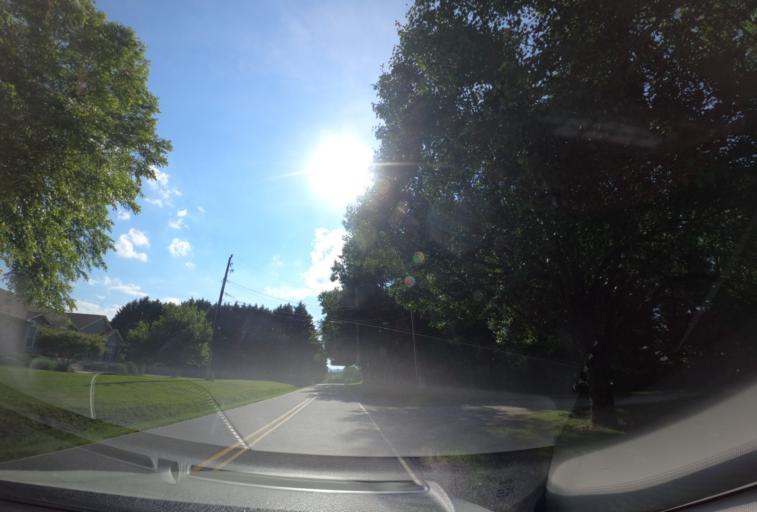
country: US
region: North Carolina
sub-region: Transylvania County
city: Brevard
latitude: 35.2579
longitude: -82.6641
